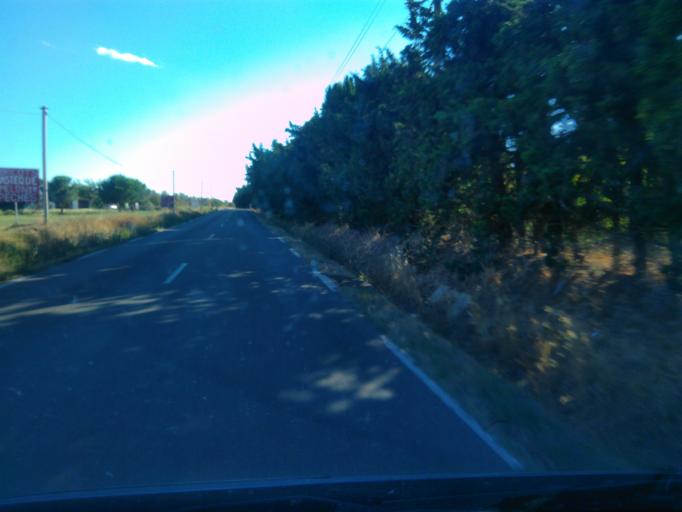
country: FR
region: Languedoc-Roussillon
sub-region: Departement du Gard
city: Saint-Gilles
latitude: 43.6642
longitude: 4.3665
